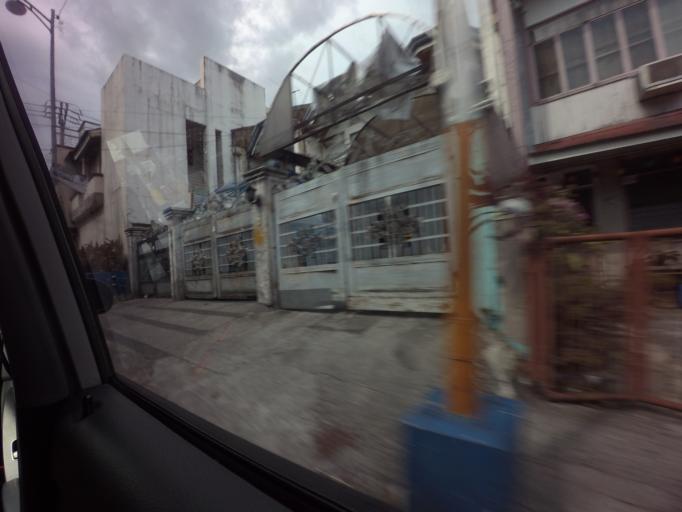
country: PH
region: Metro Manila
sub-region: City of Manila
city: Quiapo
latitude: 14.6033
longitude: 121.0082
